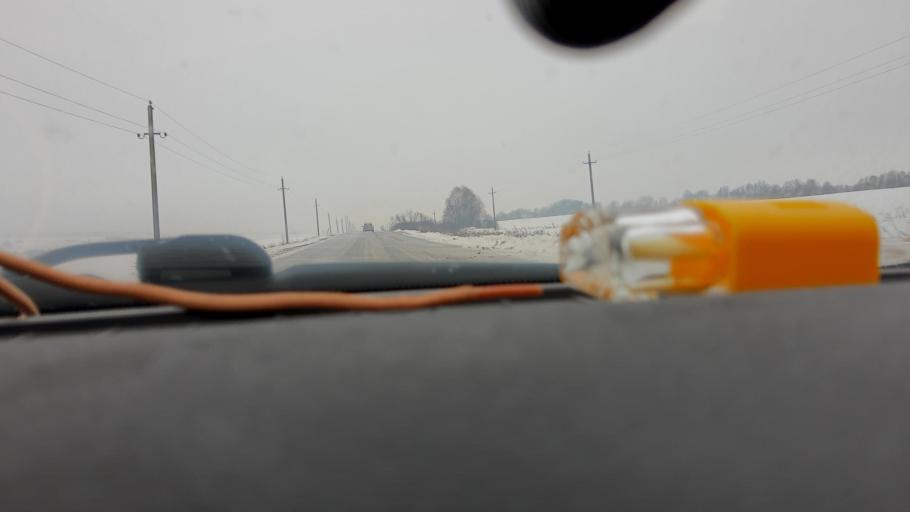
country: RU
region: Bashkortostan
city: Ulukulevo
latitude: 54.5451
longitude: 56.4333
